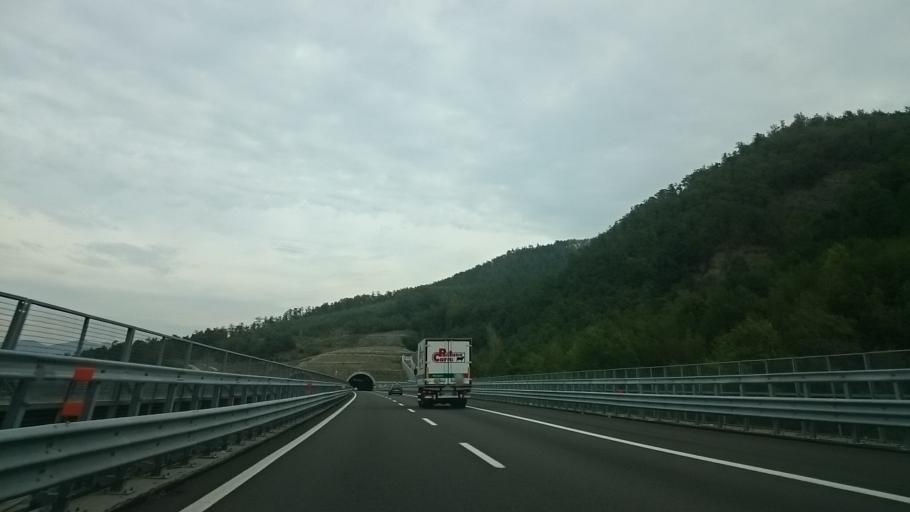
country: IT
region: Emilia-Romagna
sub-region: Provincia di Bologna
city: San Benedetto Val di Sambro
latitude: 44.1913
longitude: 11.2002
